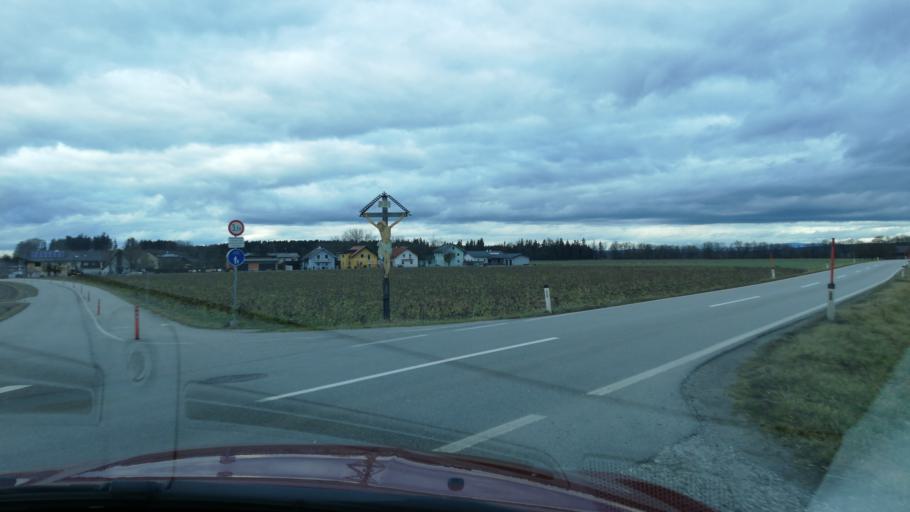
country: AT
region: Upper Austria
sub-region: Politischer Bezirk Braunau am Inn
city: Altheim
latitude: 48.2681
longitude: 13.3014
